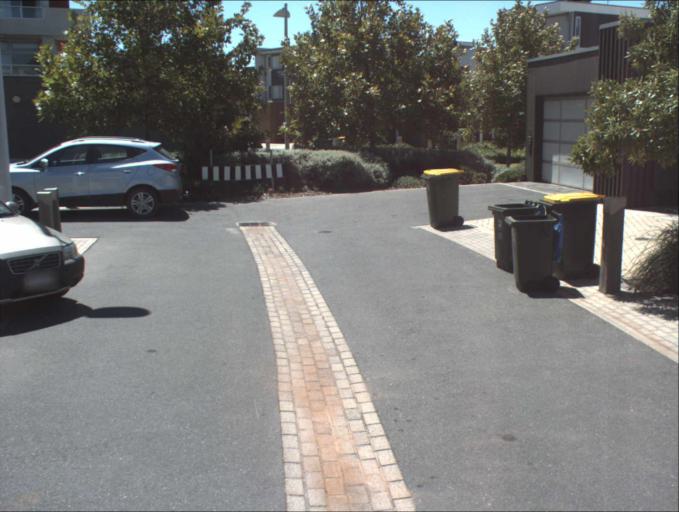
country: AU
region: South Australia
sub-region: Port Adelaide Enfield
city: Birkenhead
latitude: -34.8492
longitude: 138.4960
